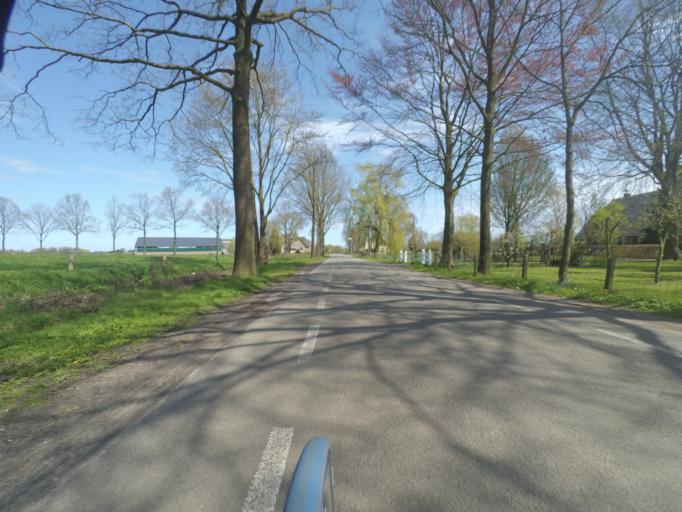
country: NL
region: Gelderland
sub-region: Gemeente Epe
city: Emst
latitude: 52.3343
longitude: 5.9662
